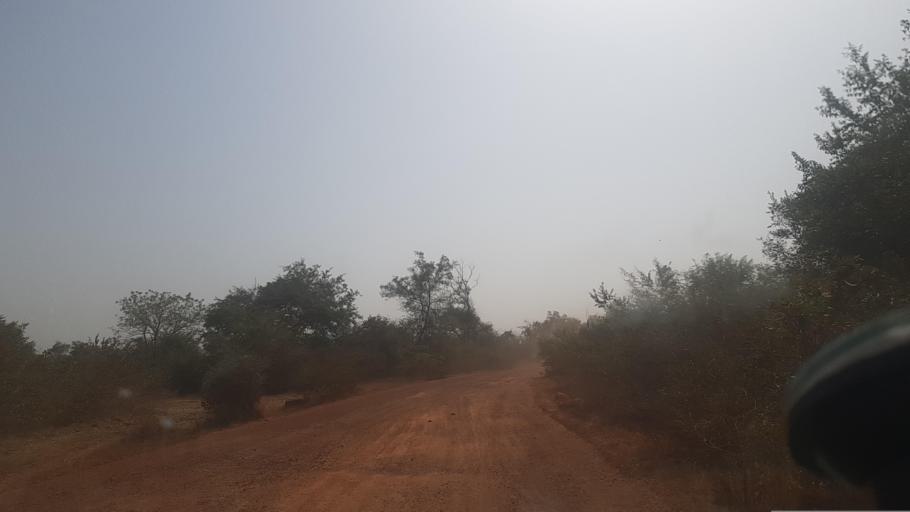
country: ML
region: Segou
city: Baroueli
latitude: 13.0742
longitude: -6.4815
